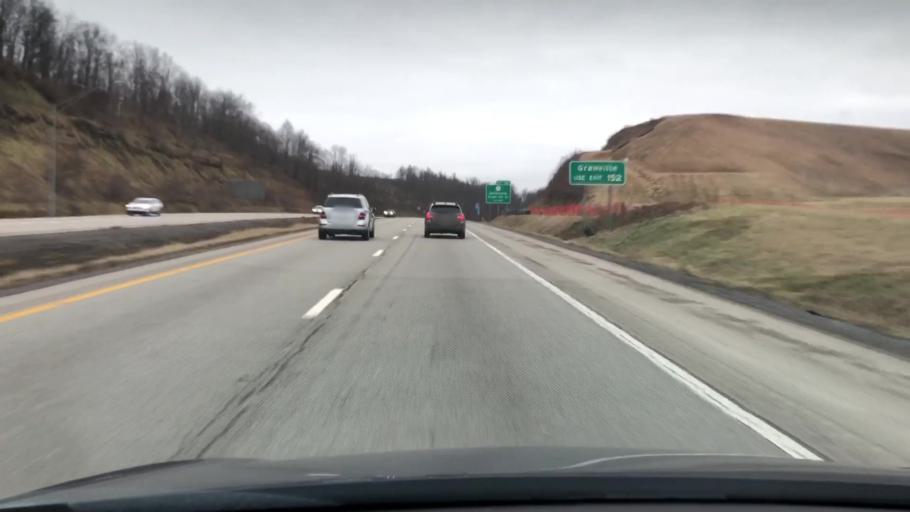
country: US
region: West Virginia
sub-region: Monongalia County
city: Star City
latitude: 39.6522
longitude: -80.0088
